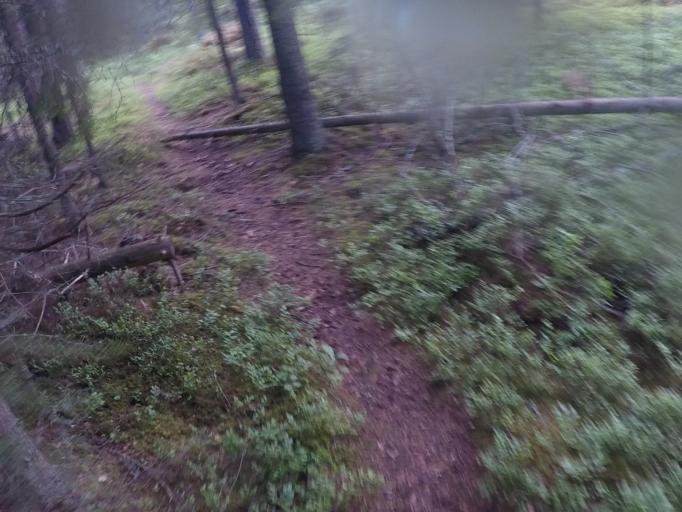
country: SE
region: Soedermanland
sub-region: Eskilstuna Kommun
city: Hallbybrunn
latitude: 59.3980
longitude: 16.3849
